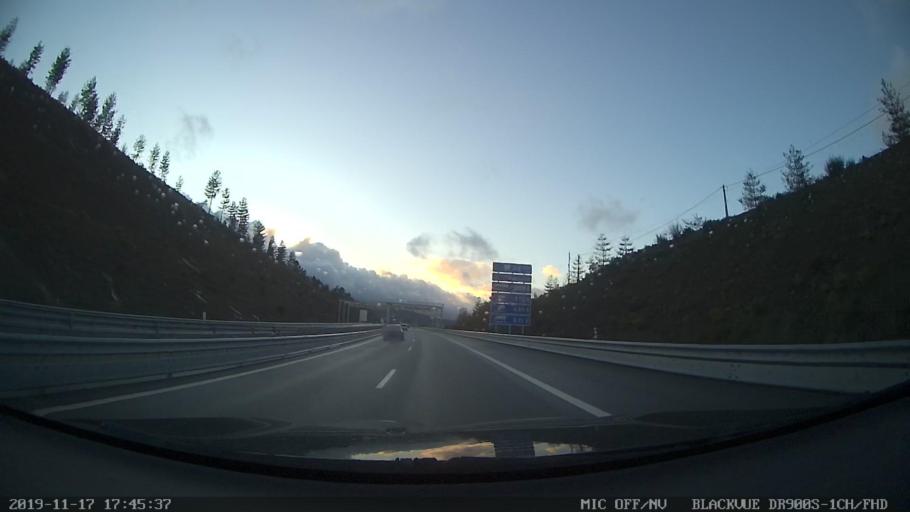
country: PT
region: Vila Real
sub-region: Santa Marta de Penaguiao
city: Santa Marta de Penaguiao
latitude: 41.2791
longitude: -7.8406
